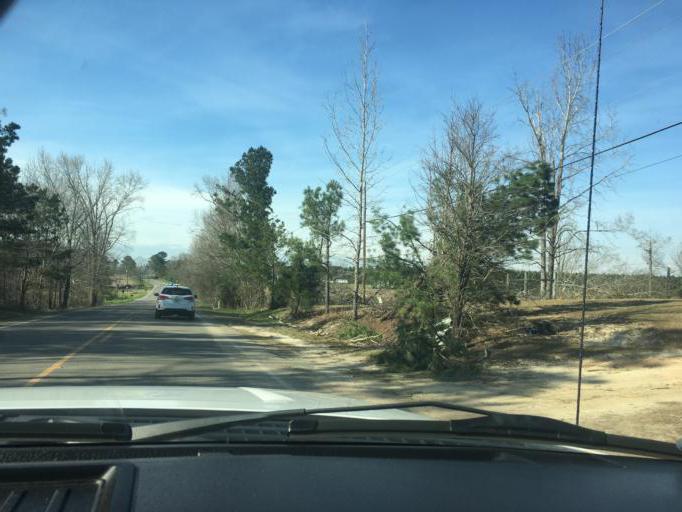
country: US
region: Alabama
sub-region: Lee County
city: Opelika
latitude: 32.4784
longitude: -85.3677
